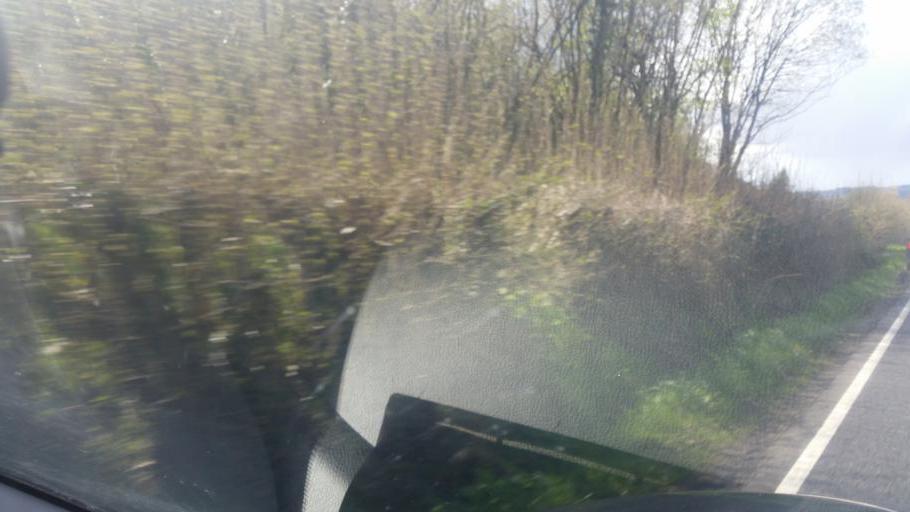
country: GB
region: Northern Ireland
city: Irvinestown
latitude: 54.4355
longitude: -7.7848
